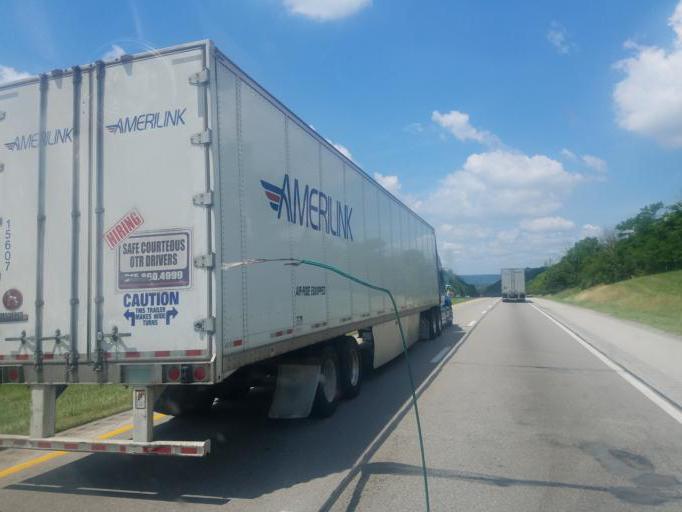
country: US
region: Kentucky
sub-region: Carroll County
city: Carrollton
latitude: 38.6532
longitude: -85.0983
